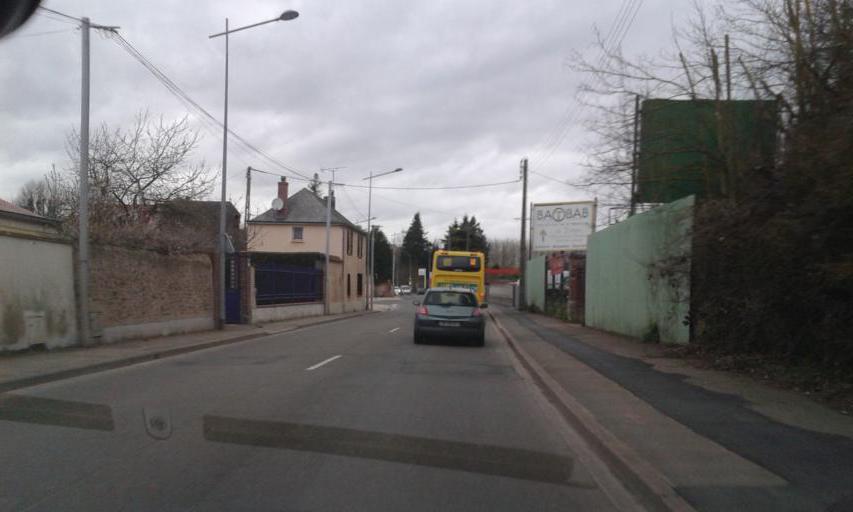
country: FR
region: Centre
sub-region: Departement d'Eure-et-Loir
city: Leves
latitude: 48.4625
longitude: 1.4819
